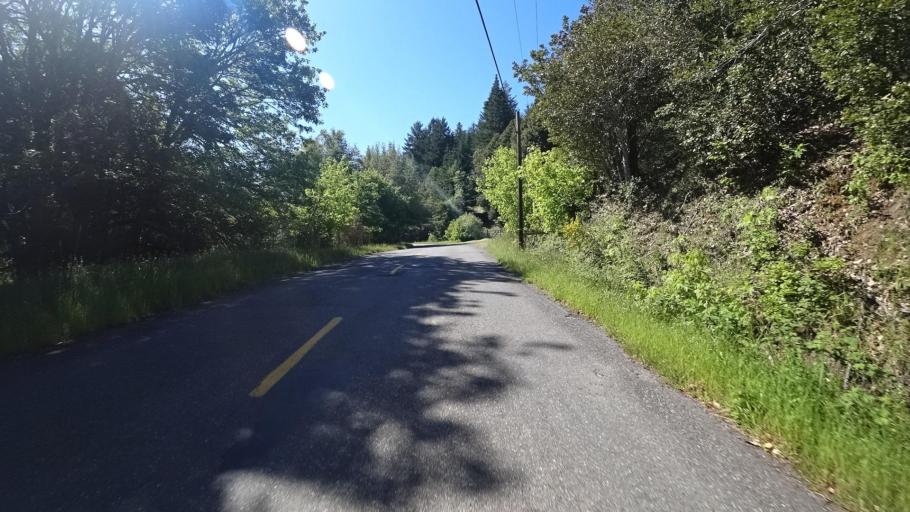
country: US
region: California
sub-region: Humboldt County
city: Rio Dell
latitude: 40.2636
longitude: -124.1968
